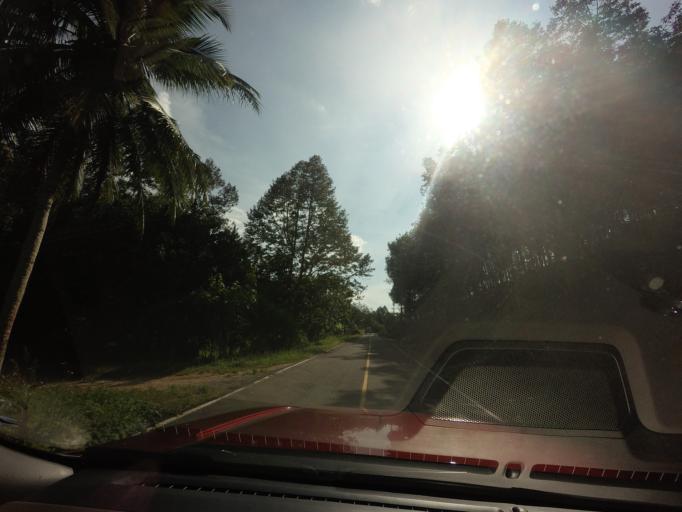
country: TH
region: Narathiwat
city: Si Sakhon
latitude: 6.0610
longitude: 101.3922
